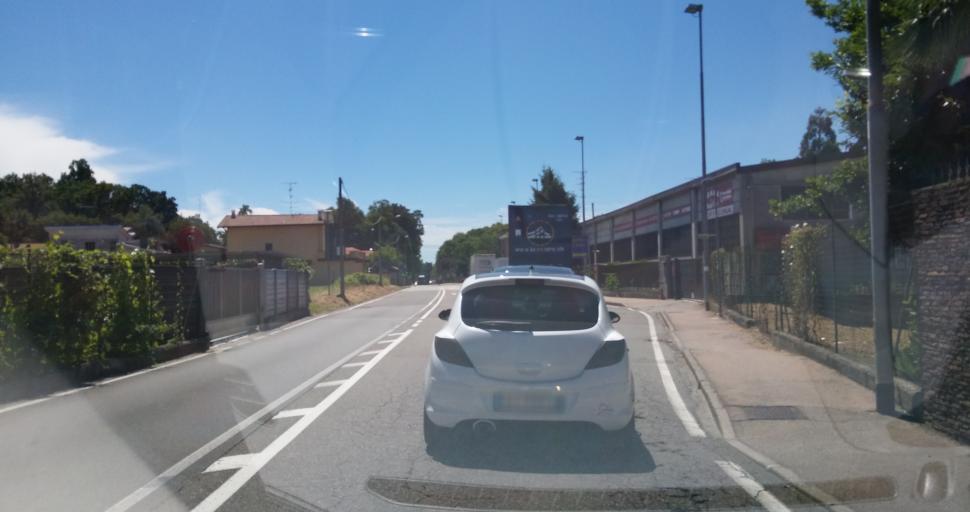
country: IT
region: Lombardy
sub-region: Provincia di Varese
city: Somma Lombardo
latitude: 45.6896
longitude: 8.7022
